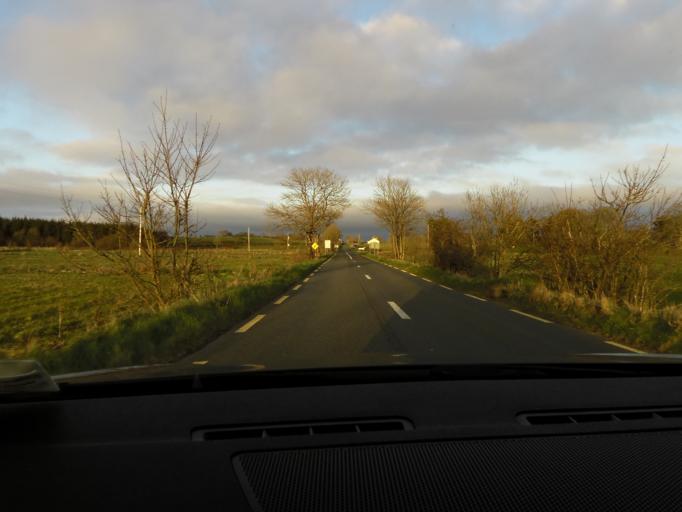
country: IE
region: Connaught
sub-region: Sligo
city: Tobercurry
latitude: 54.0449
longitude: -8.6328
